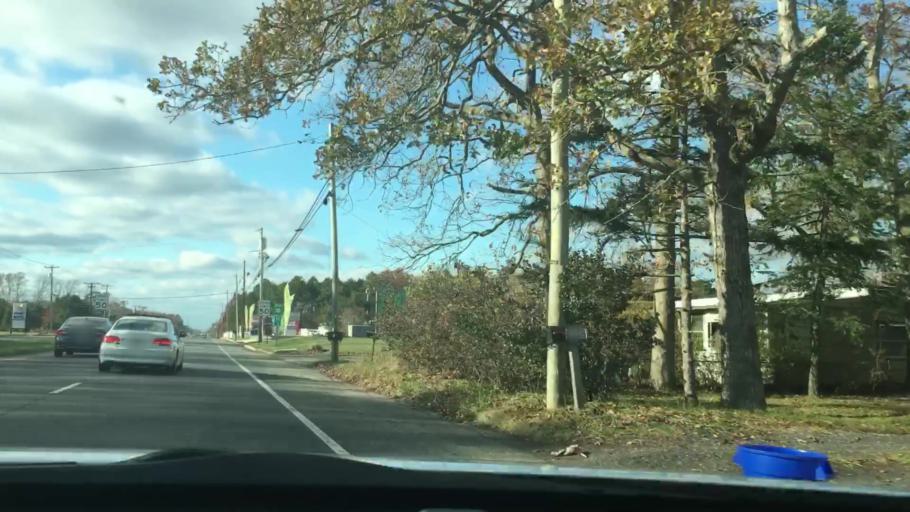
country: US
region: New Jersey
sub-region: Atlantic County
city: Pomona
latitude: 39.4195
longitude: -74.5842
